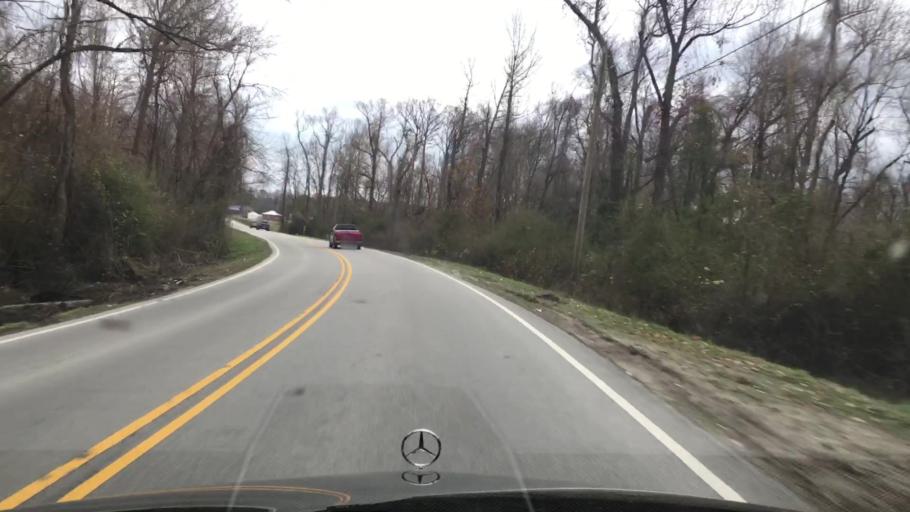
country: US
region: North Carolina
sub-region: Onslow County
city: Richlands
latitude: 34.8802
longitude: -77.5215
